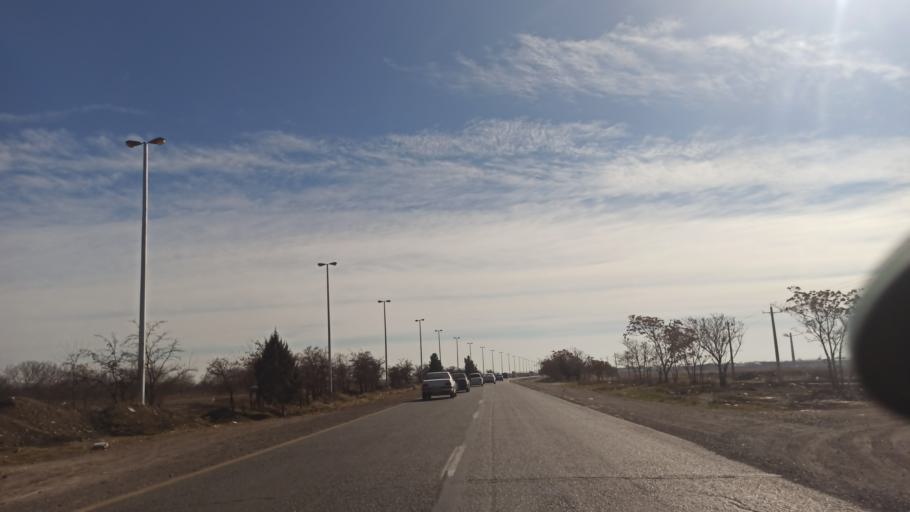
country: IR
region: Qazvin
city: Qazvin
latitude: 36.2244
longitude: 50.0084
